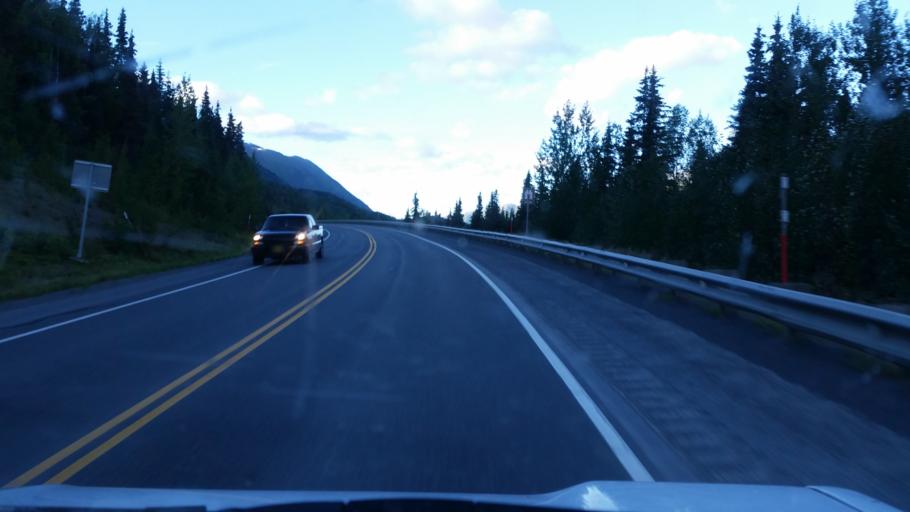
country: US
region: Alaska
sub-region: Kenai Peninsula Borough
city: Bear Creek
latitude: 60.5077
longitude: -149.6860
